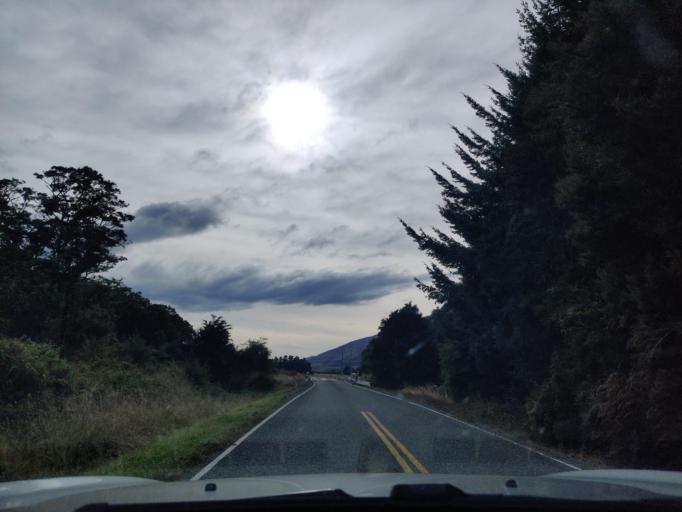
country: NZ
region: Tasman
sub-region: Tasman District
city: Wakefield
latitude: -41.7688
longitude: 172.9583
